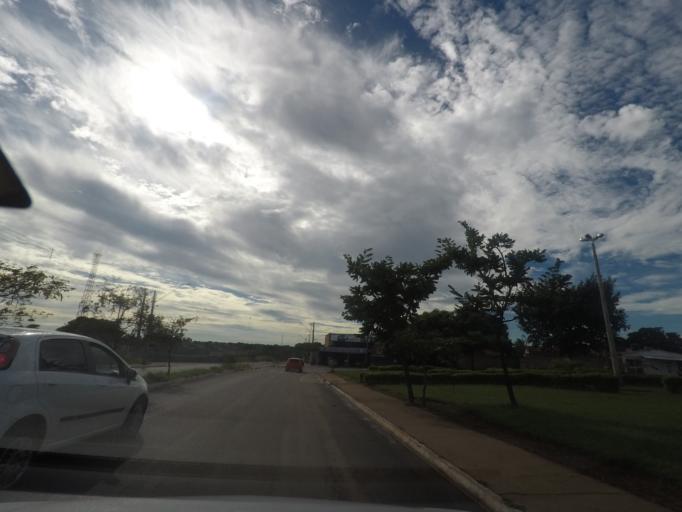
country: BR
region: Goias
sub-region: Aparecida De Goiania
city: Aparecida de Goiania
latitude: -16.8167
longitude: -49.3096
